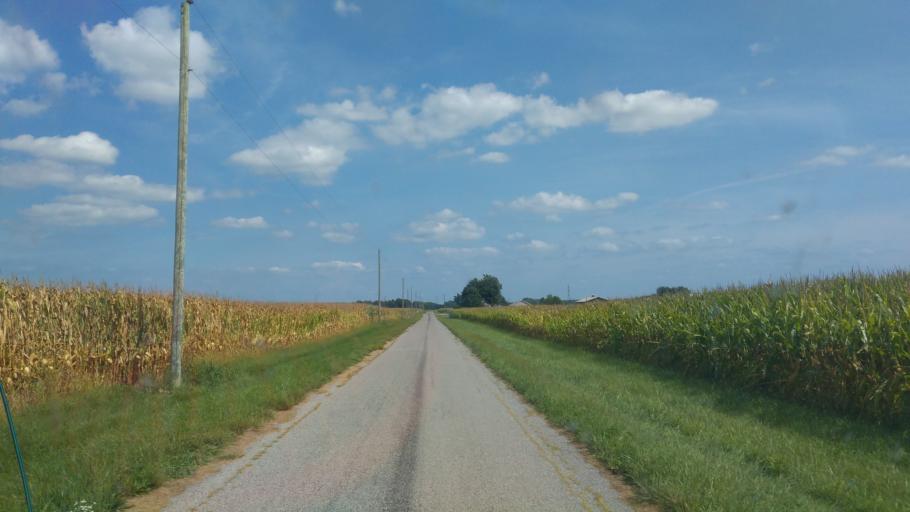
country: US
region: Ohio
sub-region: Union County
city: Richwood
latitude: 40.3966
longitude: -83.4355
